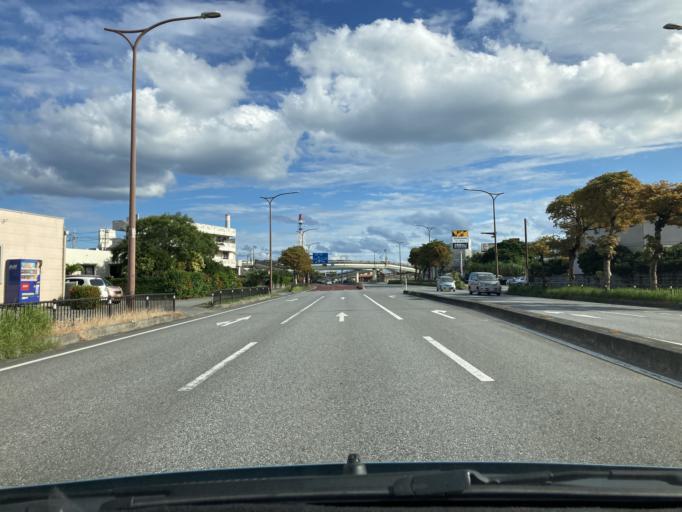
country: JP
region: Okinawa
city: Ishikawa
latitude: 26.4339
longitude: 127.8295
